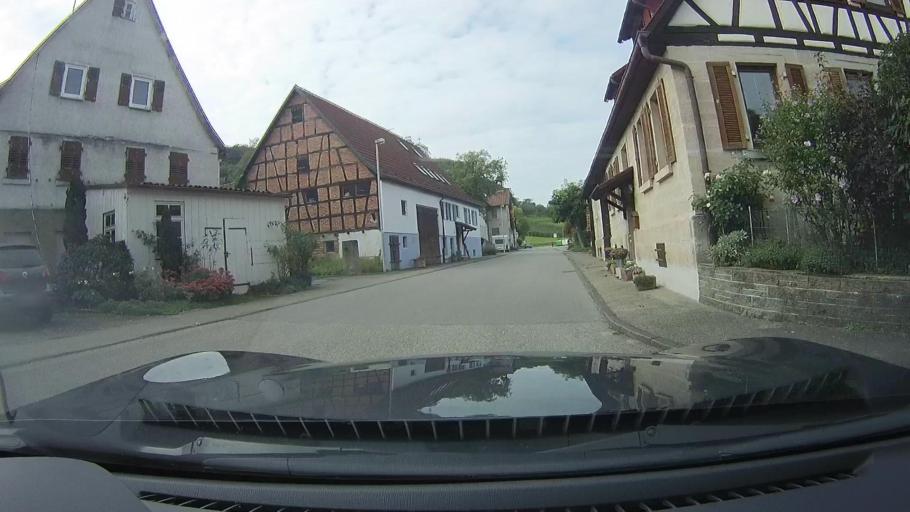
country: DE
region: Baden-Wuerttemberg
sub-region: Regierungsbezirk Stuttgart
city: Lowenstein
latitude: 49.0619
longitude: 9.3665
